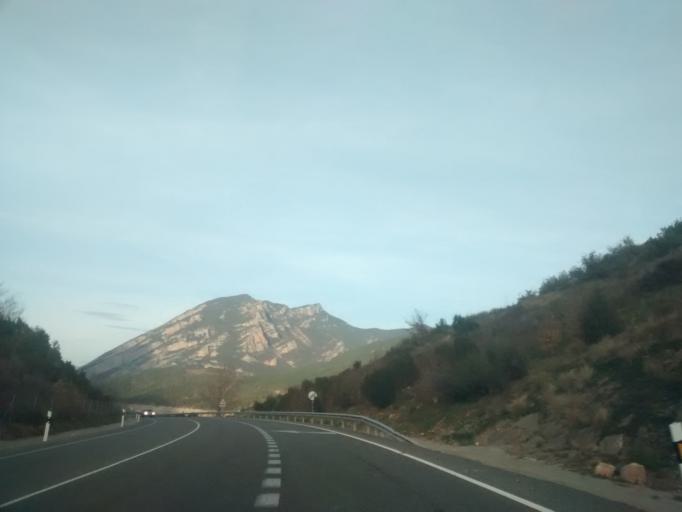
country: ES
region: Catalonia
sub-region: Provincia de Lleida
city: Oliana
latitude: 42.1027
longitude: 1.2979
